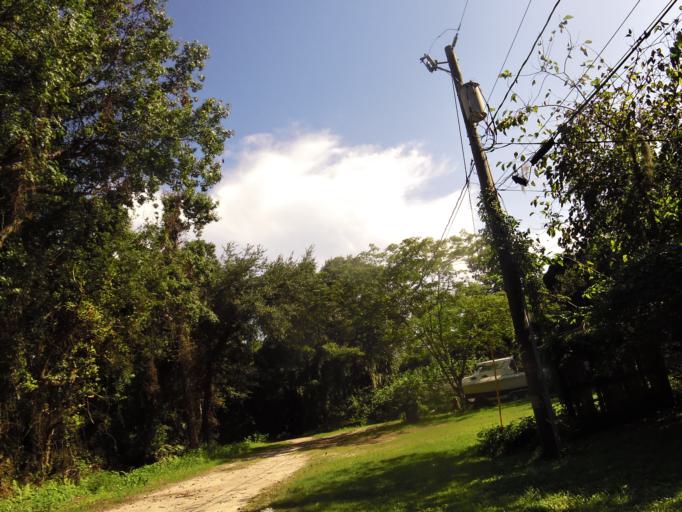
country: US
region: Florida
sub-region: Nassau County
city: Fernandina Beach
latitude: 30.6539
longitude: -81.4648
